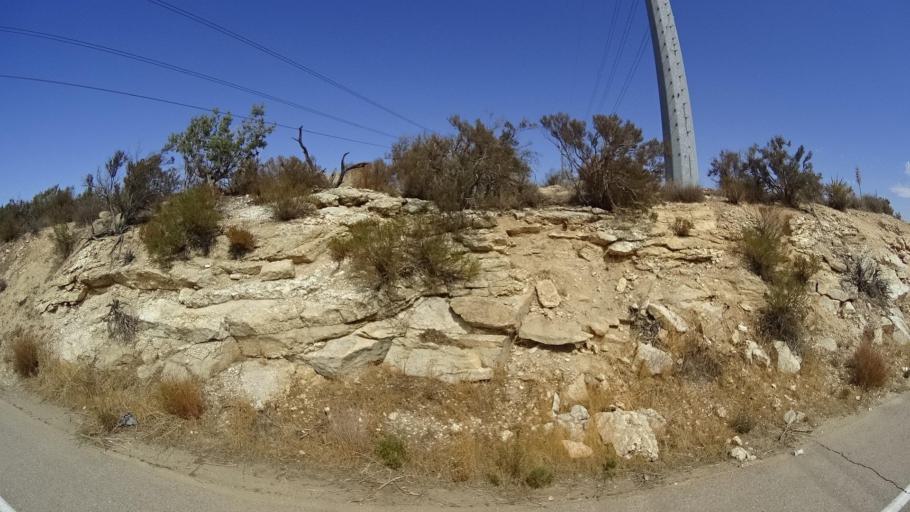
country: MX
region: Baja California
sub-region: Tecate
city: Cereso del Hongo
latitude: 32.6207
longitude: -116.2171
